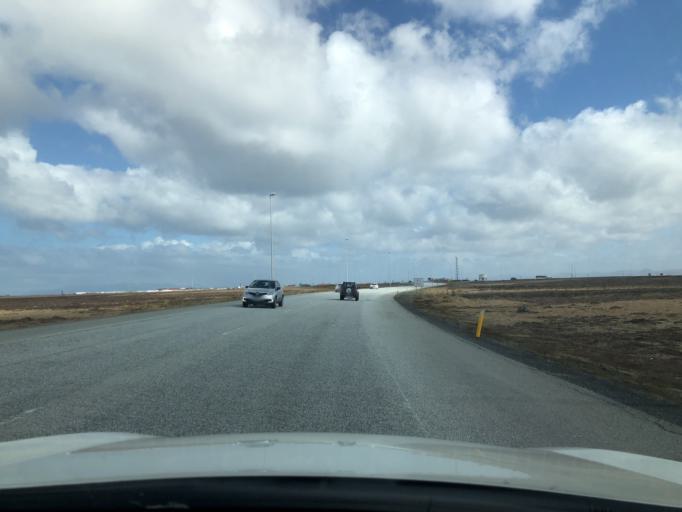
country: IS
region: Southern Peninsula
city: Reykjanesbaer
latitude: 64.0025
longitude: -22.6111
